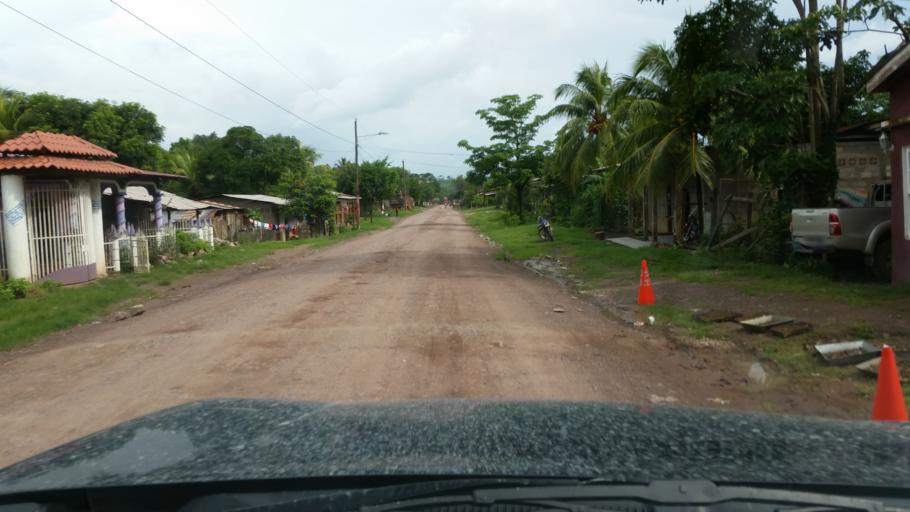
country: NI
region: Atlantico Norte (RAAN)
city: Siuna
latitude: 13.4826
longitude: -84.8444
